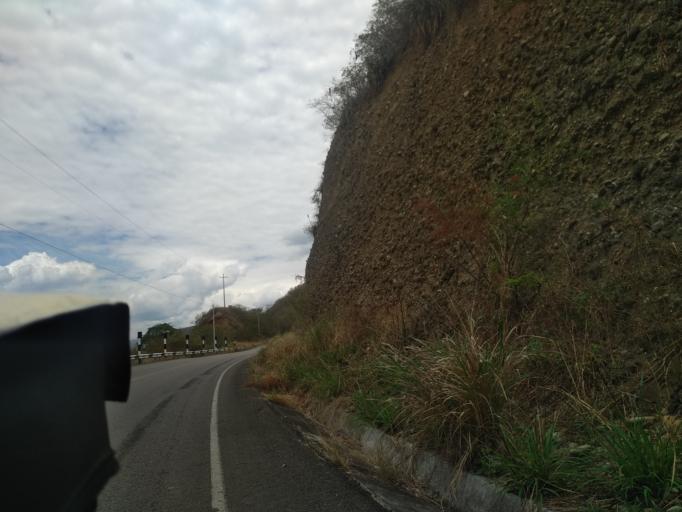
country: PE
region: Cajamarca
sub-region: Provincia de San Ignacio
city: La Coipa
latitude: -5.3899
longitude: -78.7775
